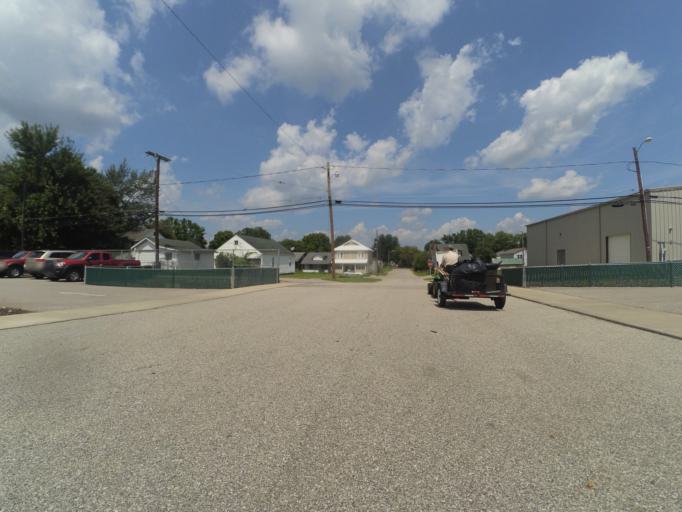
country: US
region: West Virginia
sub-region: Cabell County
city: Huntington
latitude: 38.4114
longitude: -82.4253
